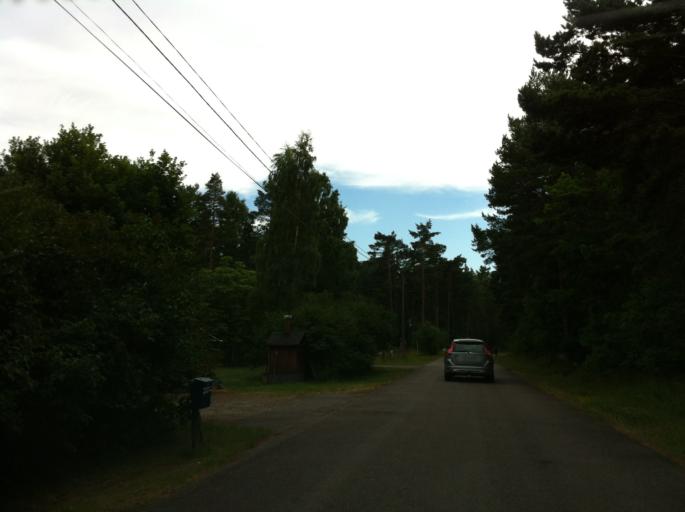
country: SE
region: Kalmar
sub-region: Vasterviks Kommun
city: Vaestervik
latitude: 57.3617
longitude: 17.0664
